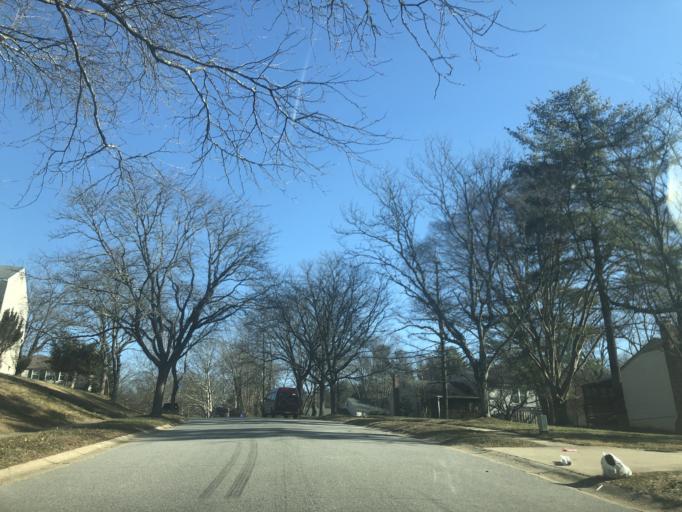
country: US
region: Maryland
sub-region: Howard County
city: Riverside
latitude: 39.1946
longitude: -76.8467
